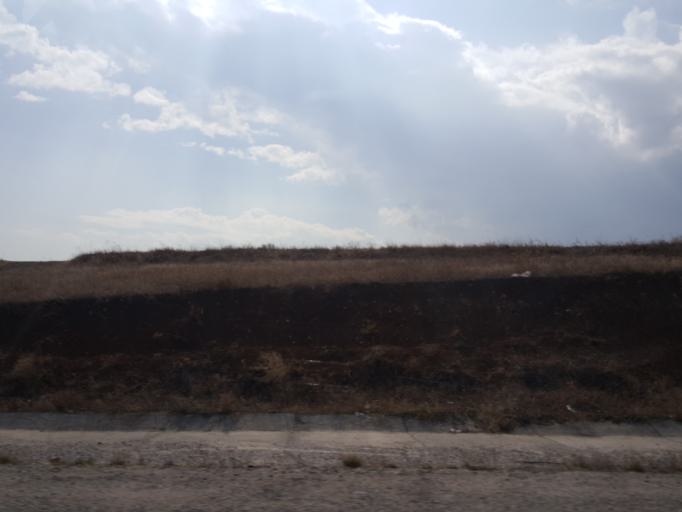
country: TR
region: Corum
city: Alaca
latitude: 40.1385
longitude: 34.7969
